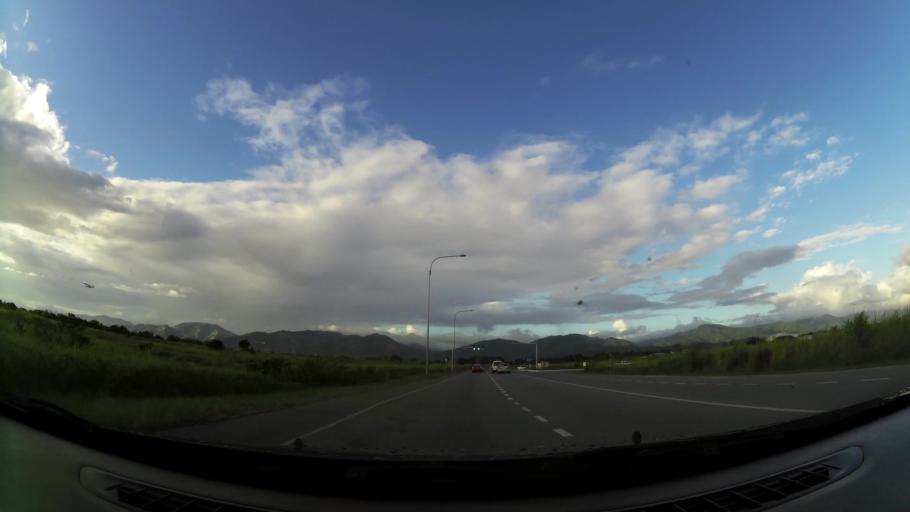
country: TT
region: Tunapuna/Piarco
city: Arouca
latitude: 10.5915
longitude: -61.3556
